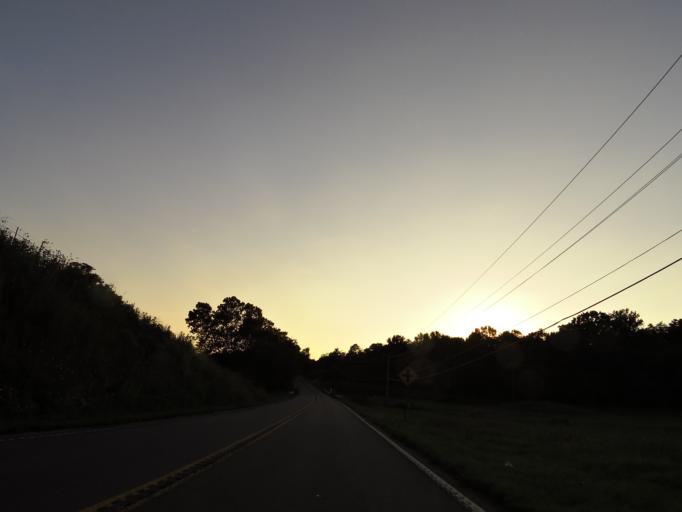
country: US
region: Tennessee
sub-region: Jefferson County
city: New Market
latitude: 36.0253
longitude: -83.5740
